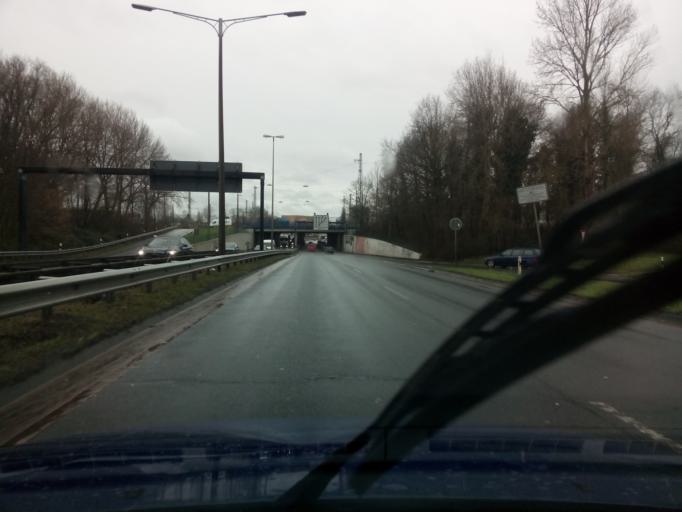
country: DE
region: Bremen
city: Bremen
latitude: 53.0971
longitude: 8.7950
